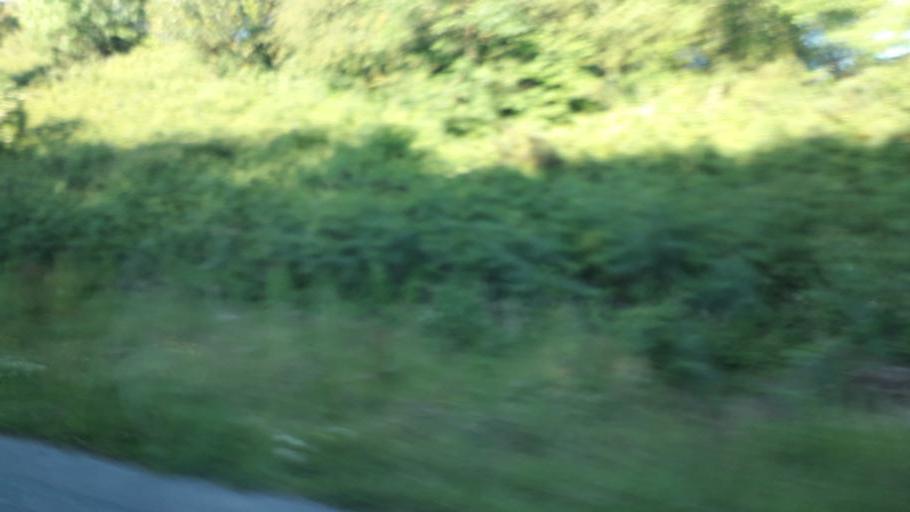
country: IE
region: Leinster
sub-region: Loch Garman
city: Loch Garman
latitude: 52.3481
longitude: -6.5139
